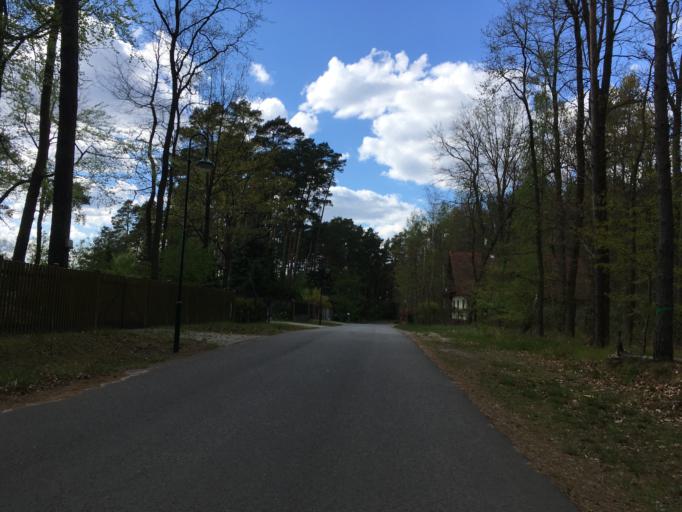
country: DE
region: Brandenburg
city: Wandlitz
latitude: 52.7630
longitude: 13.4394
